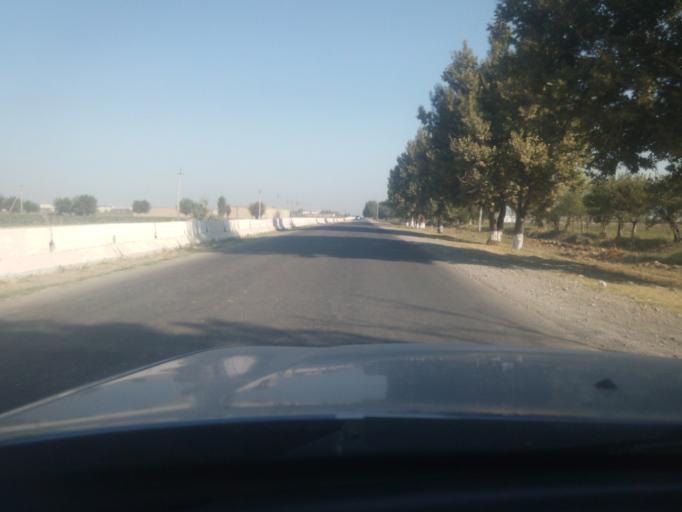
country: UZ
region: Sirdaryo
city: Guliston
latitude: 40.5033
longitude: 68.7976
